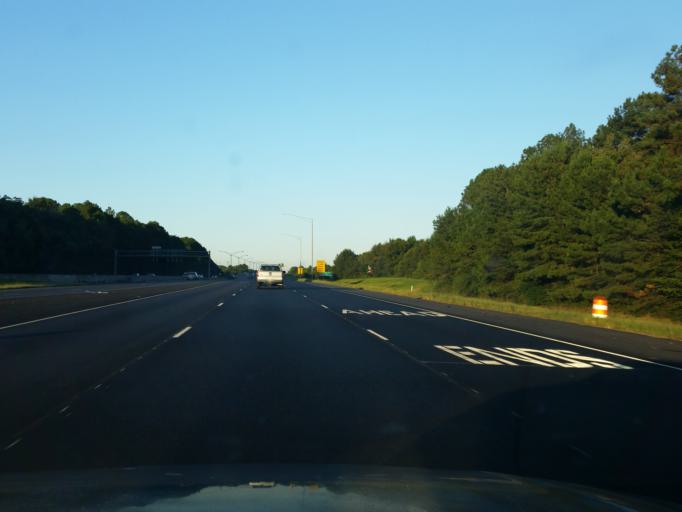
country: US
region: Alabama
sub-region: Mobile County
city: Tillmans Corner
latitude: 30.6286
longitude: -88.1129
